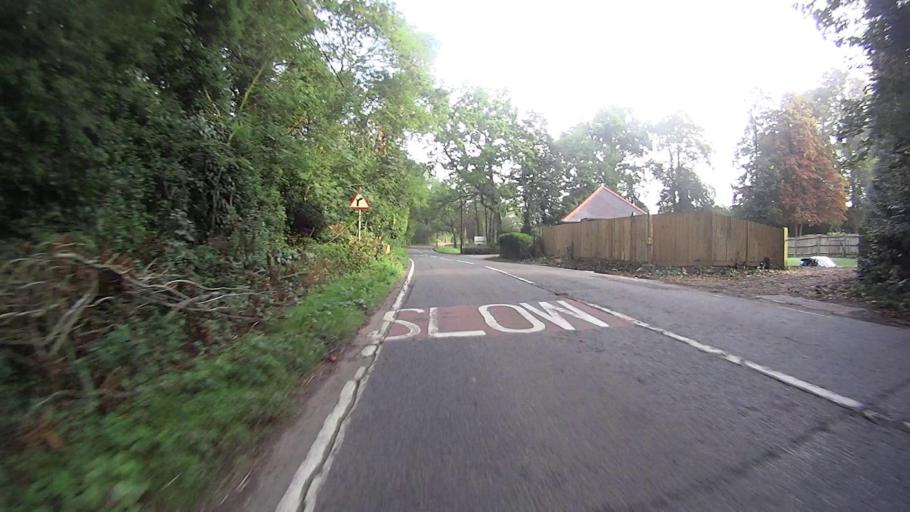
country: GB
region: England
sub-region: West Sussex
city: Copthorne
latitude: 51.1575
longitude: -0.1131
